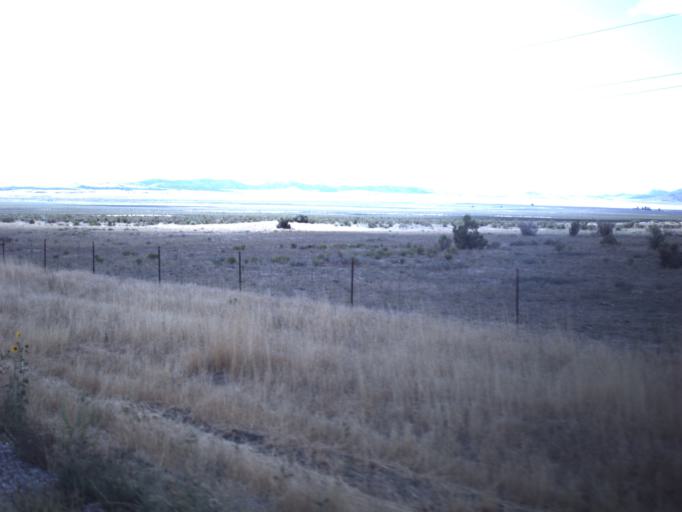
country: US
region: Utah
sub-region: Tooele County
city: Grantsville
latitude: 40.2936
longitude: -112.6564
